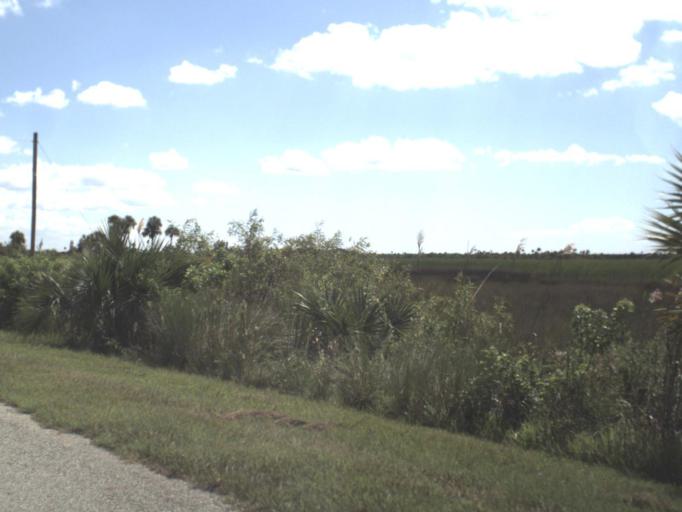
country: US
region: Florida
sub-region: Collier County
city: Marco
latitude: 25.9451
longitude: -81.4761
